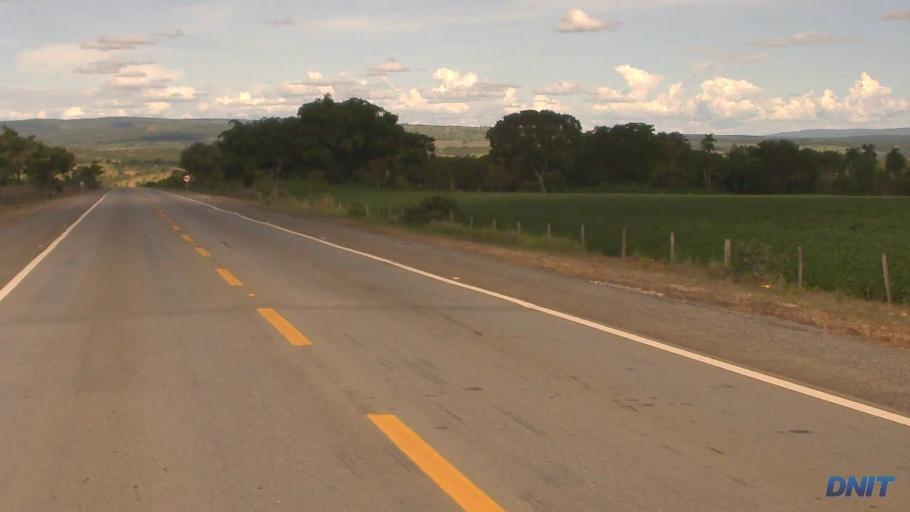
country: BR
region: Goias
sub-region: Padre Bernardo
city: Padre Bernardo
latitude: -15.2163
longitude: -48.6045
